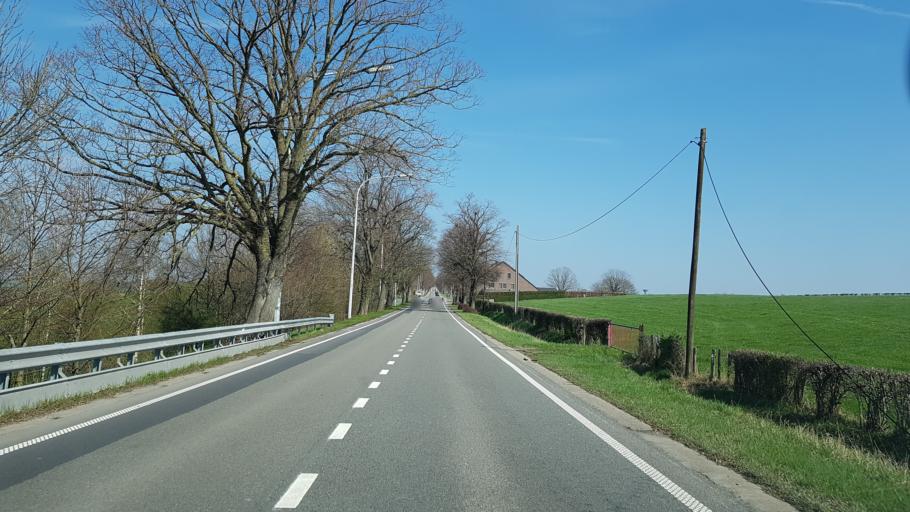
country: BE
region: Wallonia
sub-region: Province de Liege
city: Aubel
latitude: 50.6580
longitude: 5.8907
